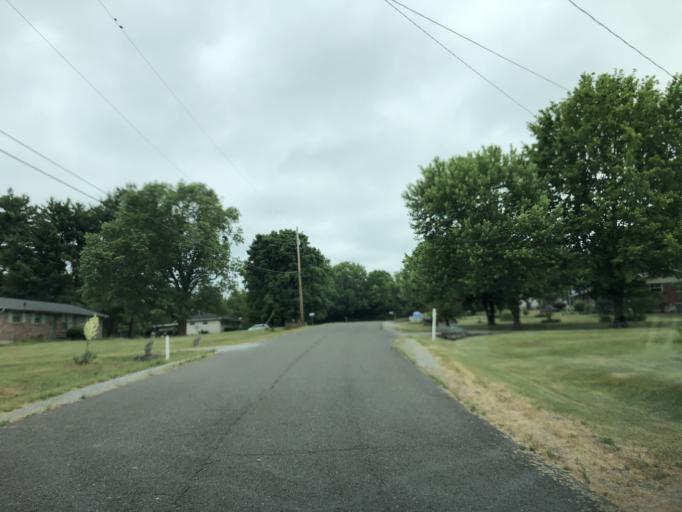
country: US
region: Tennessee
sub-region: Davidson County
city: Goodlettsville
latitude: 36.2905
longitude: -86.7269
